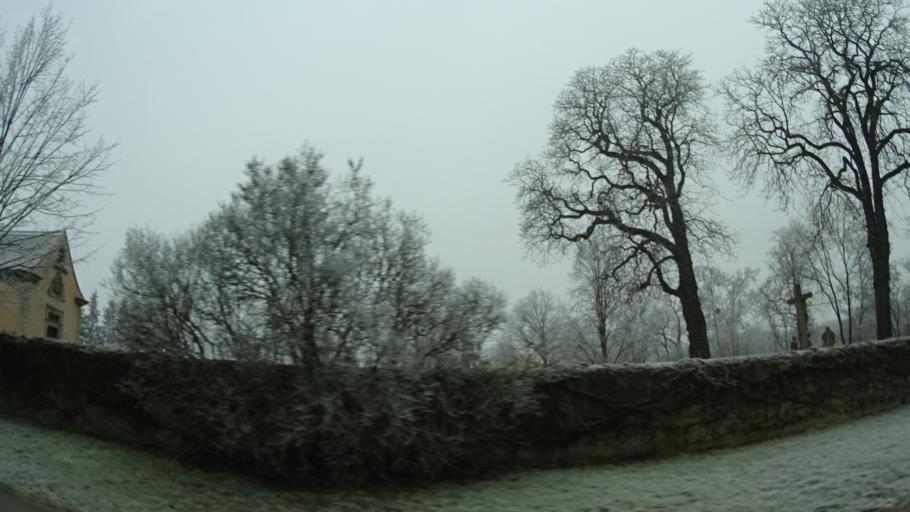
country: DE
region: Bavaria
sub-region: Regierungsbezirk Unterfranken
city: Wonfurt
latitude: 50.0093
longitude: 10.4649
